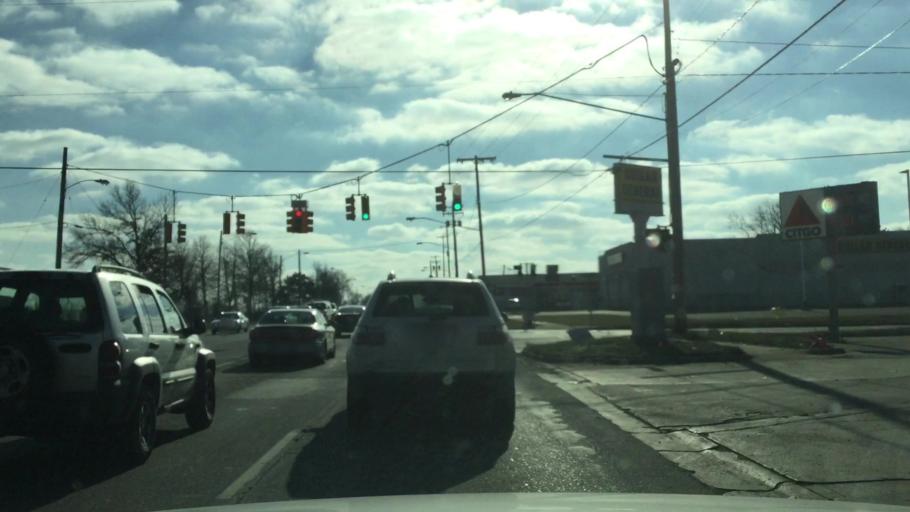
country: US
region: Michigan
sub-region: Genesee County
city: Flint
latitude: 43.0333
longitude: -83.6554
